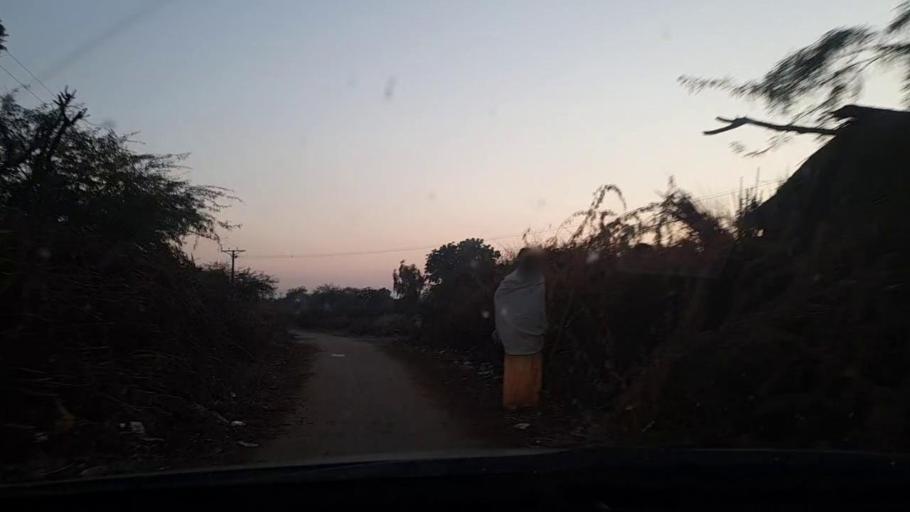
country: PK
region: Sindh
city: Tando Mittha Khan
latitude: 25.9279
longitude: 69.3313
